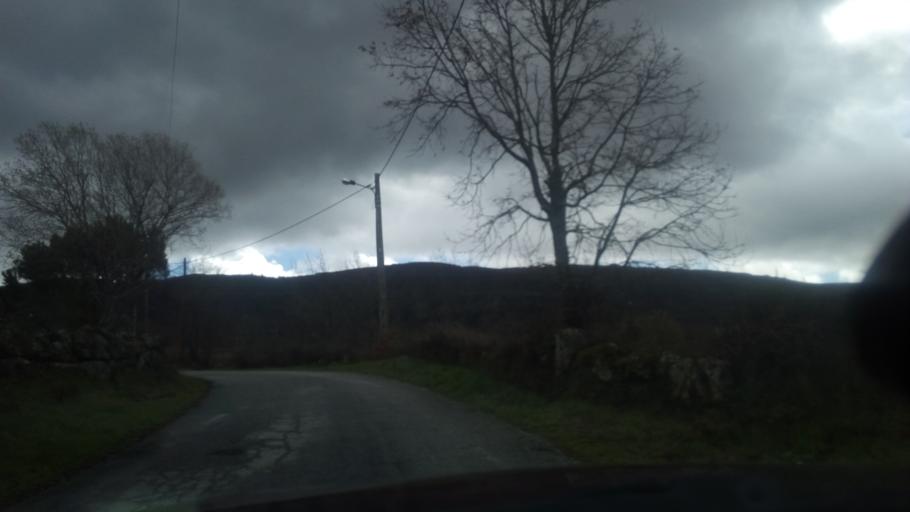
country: PT
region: Guarda
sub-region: Celorico da Beira
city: Celorico da Beira
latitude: 40.5549
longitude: -7.4589
